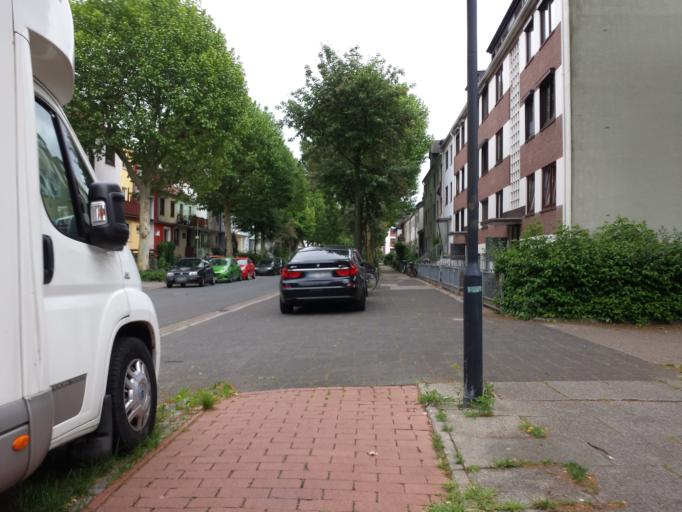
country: DE
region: Bremen
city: Bremen
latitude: 53.0976
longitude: 8.7999
